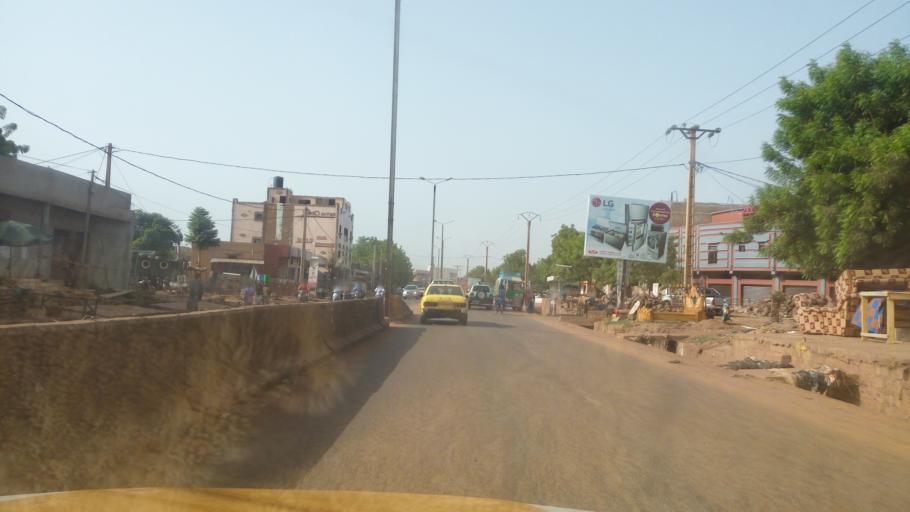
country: ML
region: Bamako
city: Bamako
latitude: 12.6013
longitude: -8.0120
